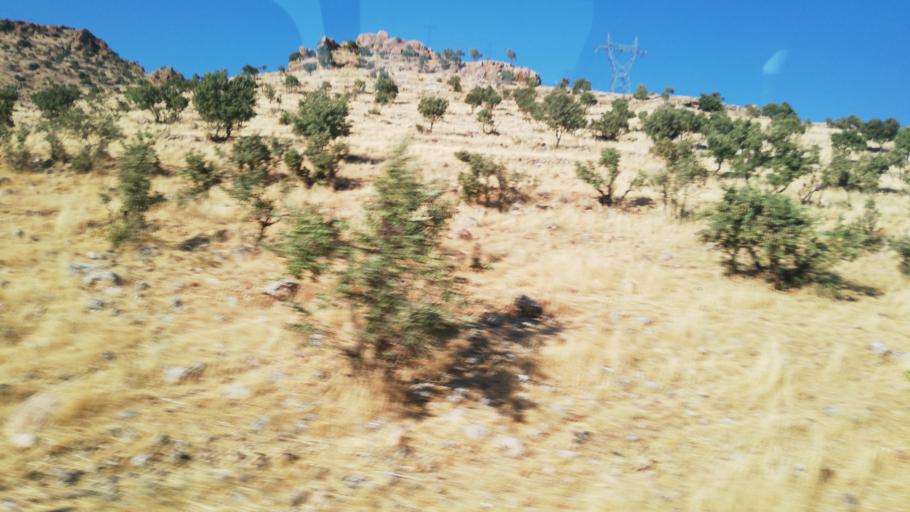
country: TR
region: Mardin
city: Sivrice
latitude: 37.2484
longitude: 41.3526
